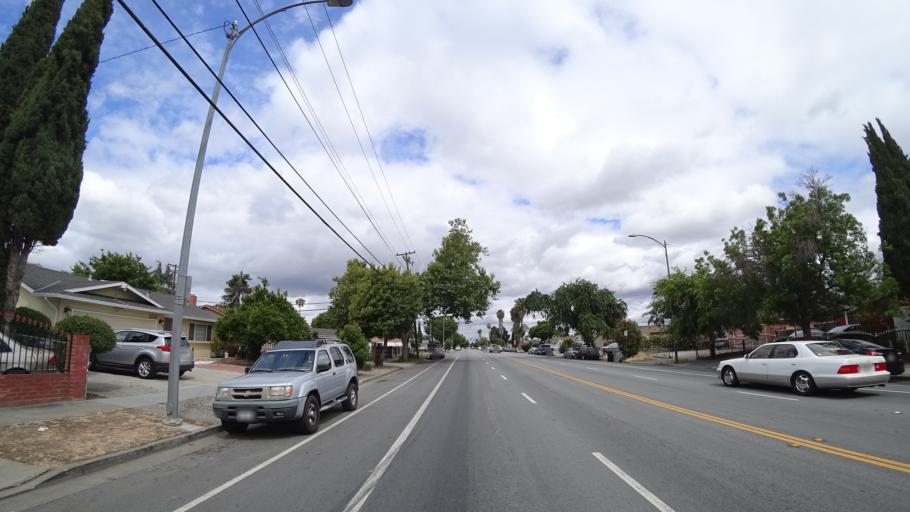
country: US
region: California
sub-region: Santa Clara County
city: Alum Rock
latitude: 37.3263
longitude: -121.8299
